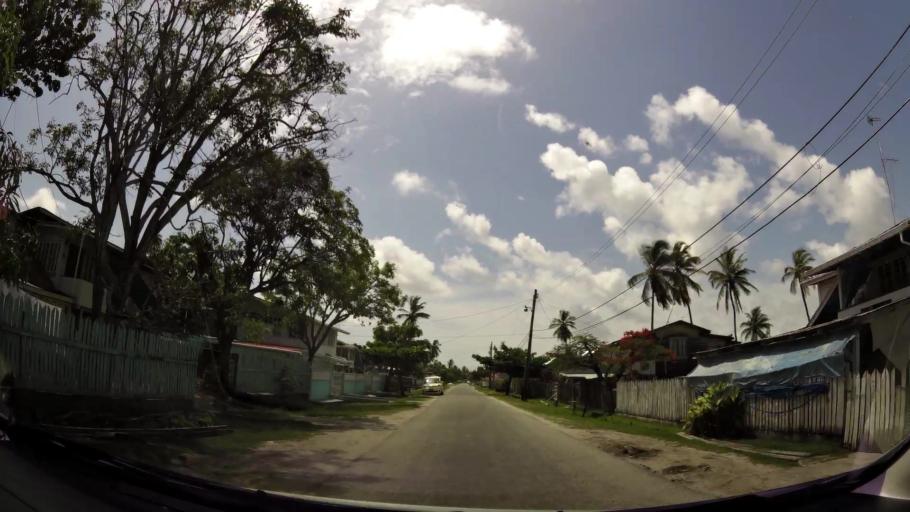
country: GY
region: Demerara-Mahaica
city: Mahaica Village
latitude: 6.7678
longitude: -58.0107
